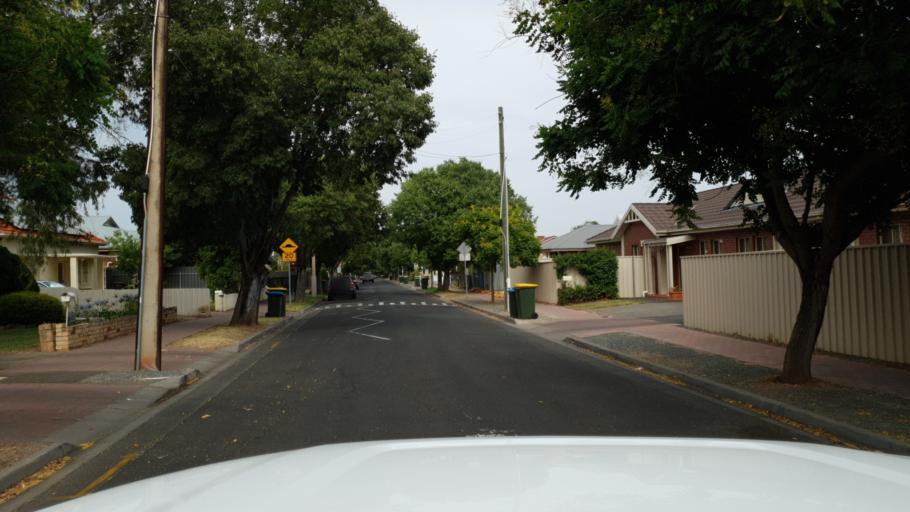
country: AU
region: South Australia
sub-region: Mitcham
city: Clarence Gardens
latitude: -34.9703
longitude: 138.5821
